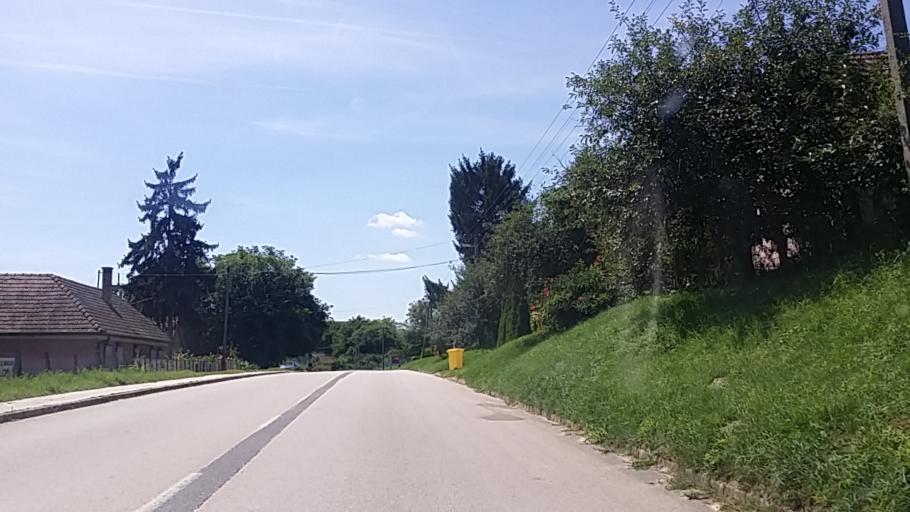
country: HU
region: Tolna
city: Iregszemcse
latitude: 46.7519
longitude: 18.1209
